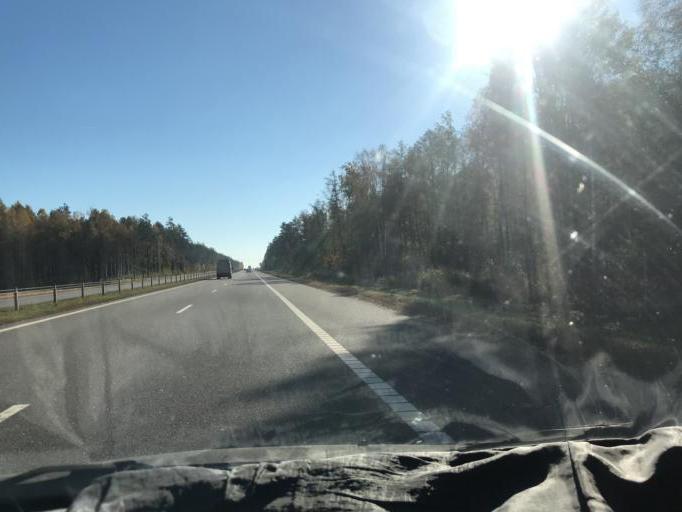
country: BY
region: Mogilev
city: Yalizava
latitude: 53.2645
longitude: 28.8879
